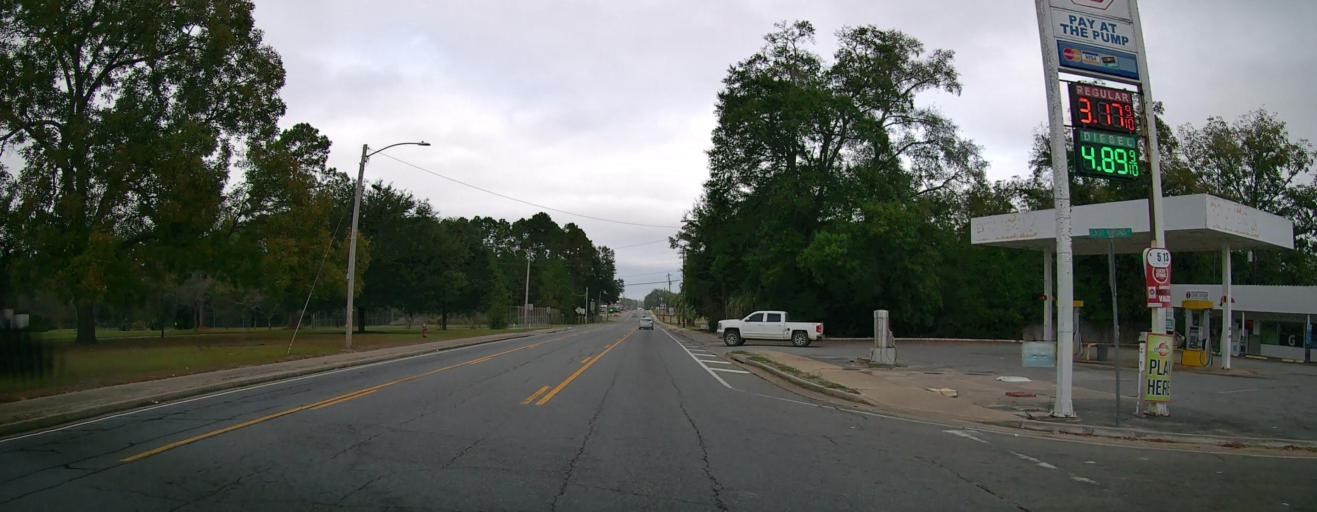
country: US
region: Georgia
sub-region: Tift County
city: Omega
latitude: 31.2700
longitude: -83.6867
